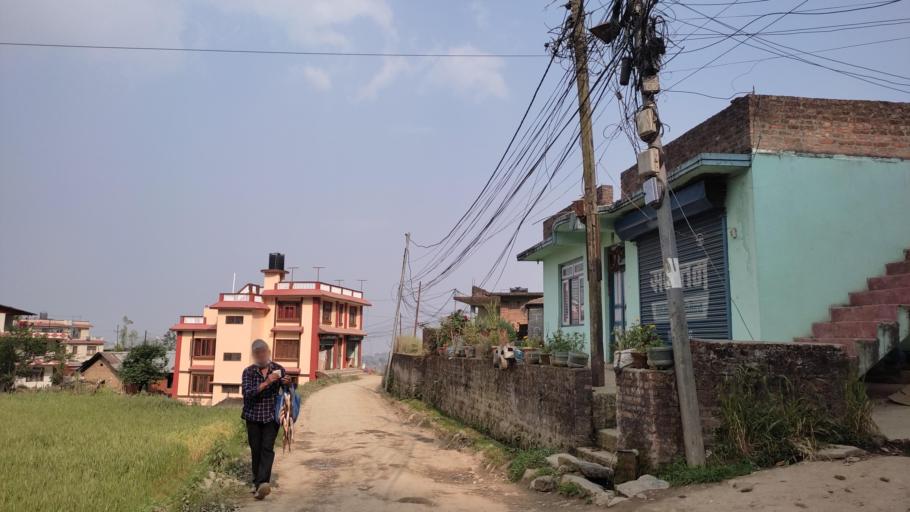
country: NP
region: Central Region
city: Kirtipur
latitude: 27.6607
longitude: 85.2594
